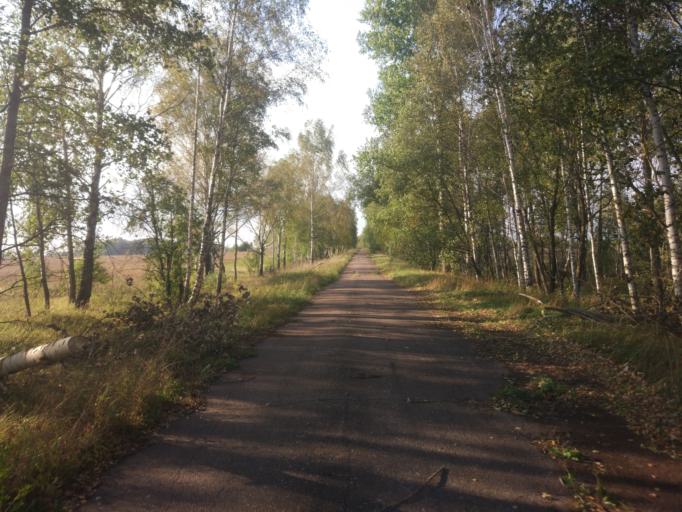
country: RU
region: Brjansk
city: Vyshkov
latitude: 52.6591
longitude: 31.5792
